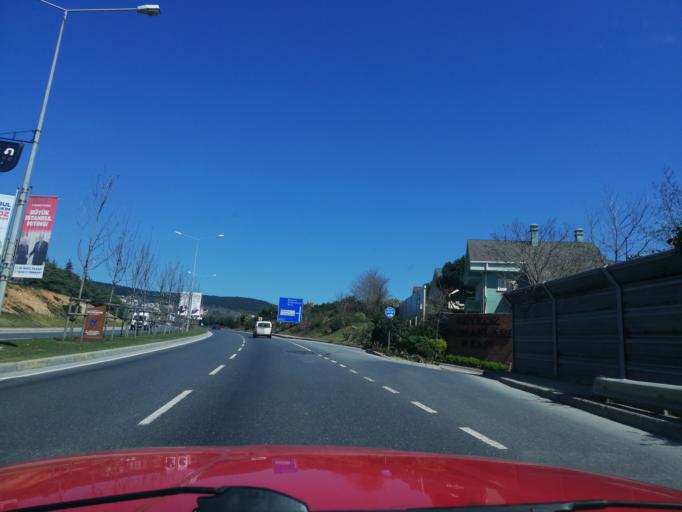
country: TR
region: Istanbul
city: Mahmut Sevket Pasa
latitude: 41.1115
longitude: 29.1178
